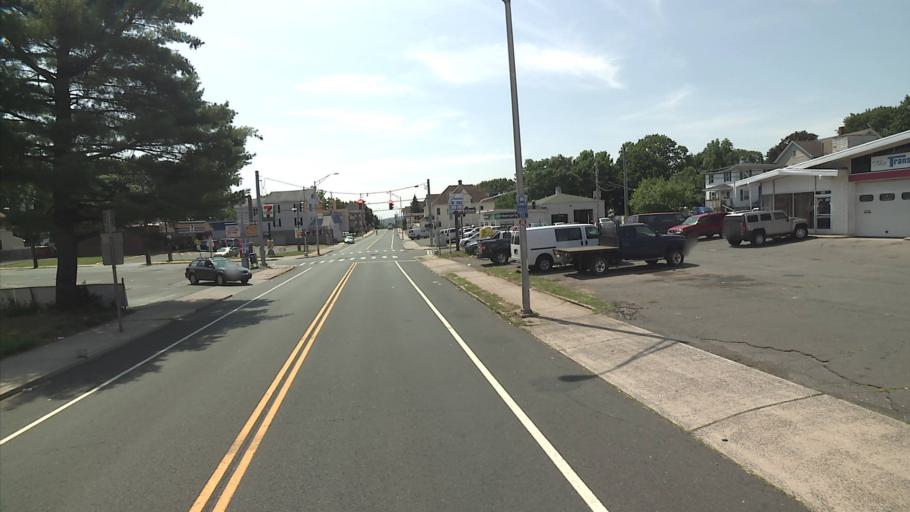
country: US
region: Connecticut
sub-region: Hartford County
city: New Britain
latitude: 41.6577
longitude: -72.7774
